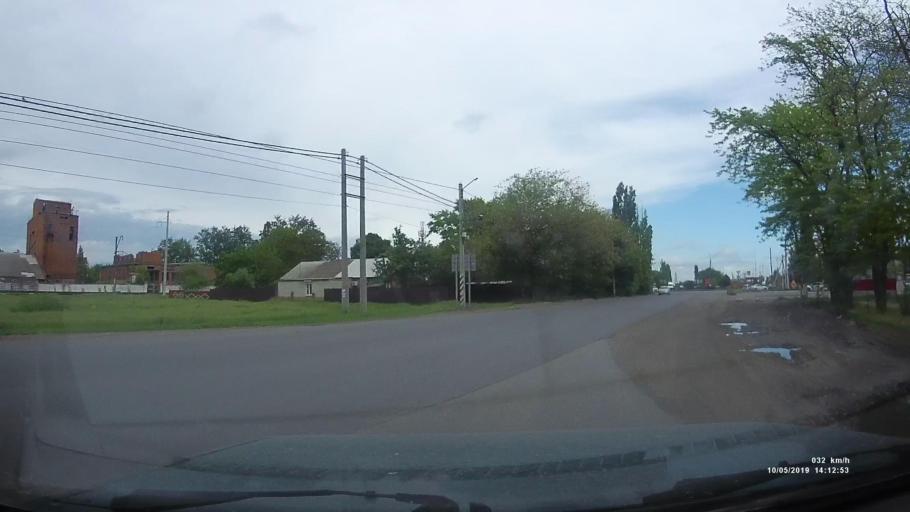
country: RU
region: Rostov
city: Azov
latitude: 47.0924
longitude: 39.4301
